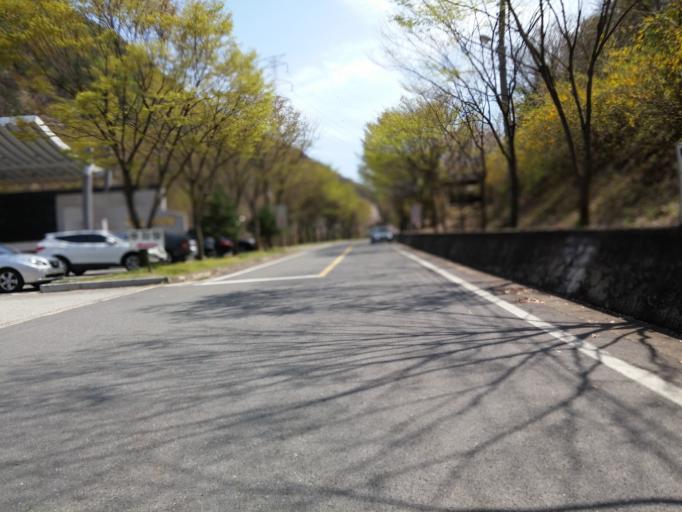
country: KR
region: Chungcheongbuk-do
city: Okcheon
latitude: 36.2419
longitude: 127.5546
